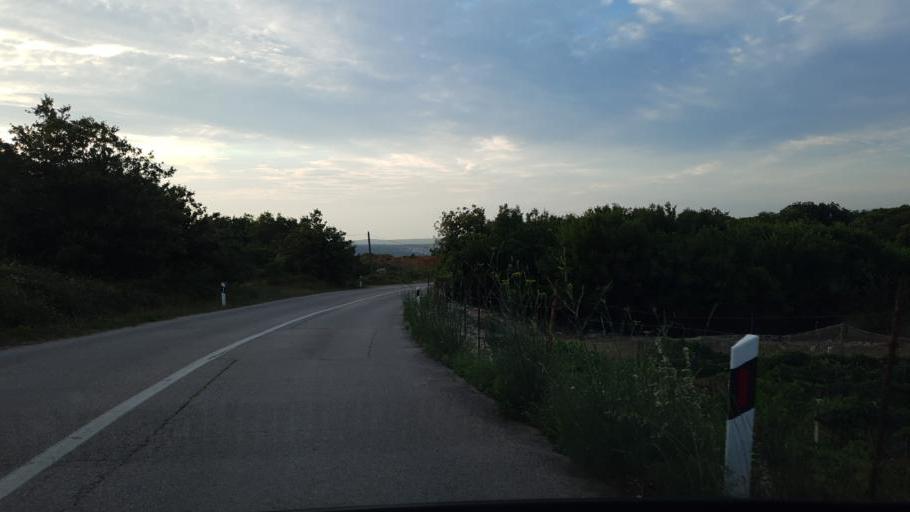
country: HR
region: Primorsko-Goranska
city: Punat
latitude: 45.0009
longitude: 14.6338
